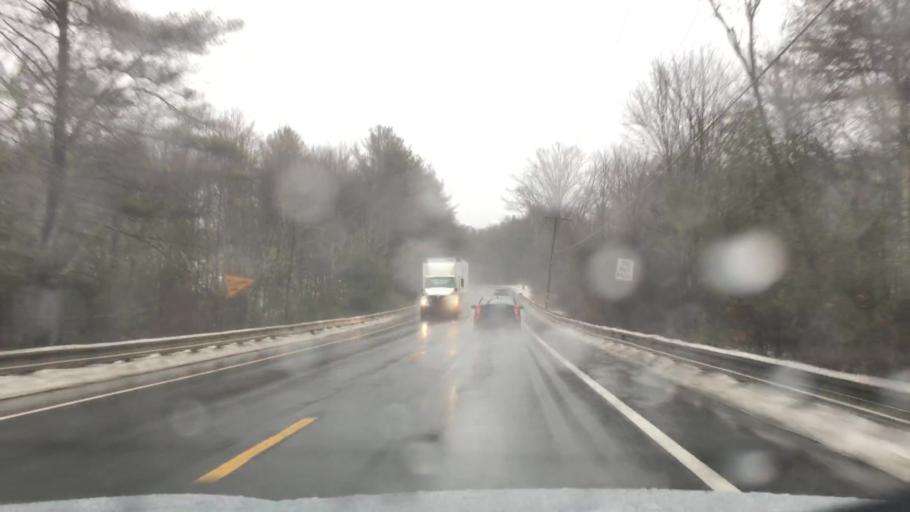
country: US
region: Massachusetts
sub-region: Franklin County
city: Shutesbury
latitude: 42.4836
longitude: -72.3431
